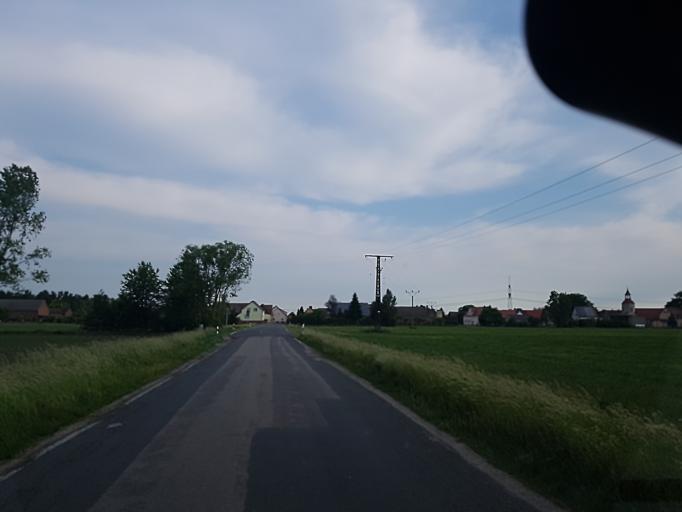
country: DE
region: Saxony-Anhalt
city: Jessen
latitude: 51.8188
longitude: 12.9505
